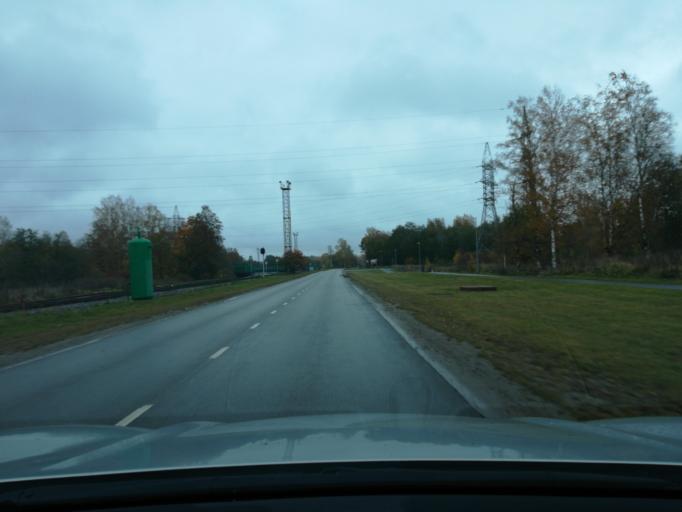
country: EE
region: Ida-Virumaa
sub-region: Johvi vald
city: Johvi
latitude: 59.3163
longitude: 27.4372
